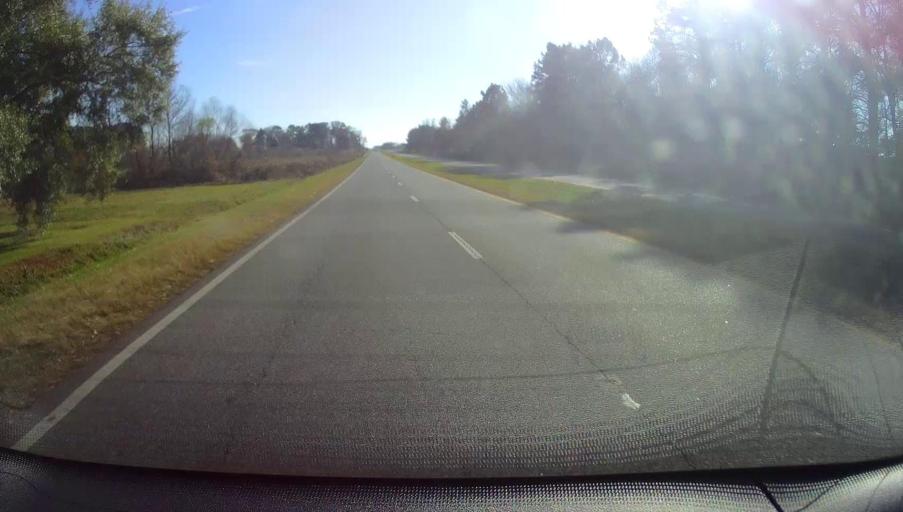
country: US
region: Alabama
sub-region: Morgan County
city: Decatur
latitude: 34.6783
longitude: -86.9497
